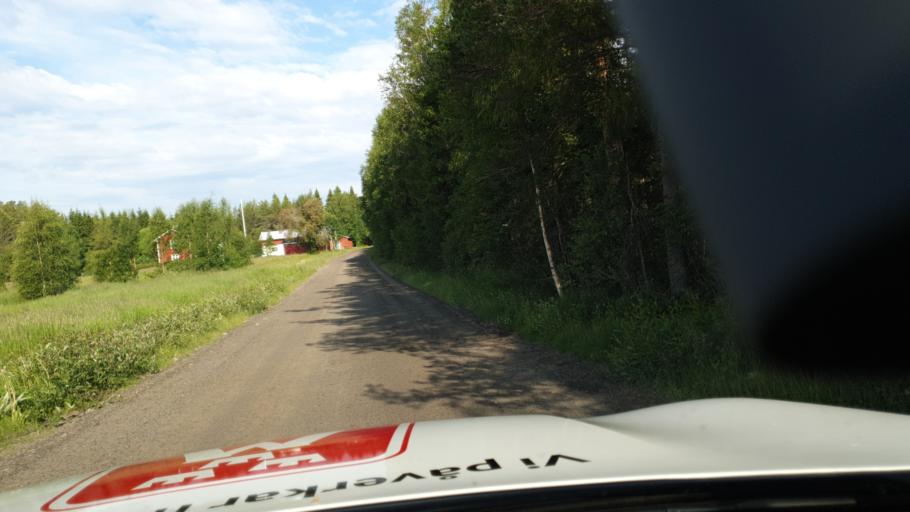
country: SE
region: Vaesterbotten
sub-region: Robertsfors Kommun
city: Robertsfors
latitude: 64.2273
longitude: 21.0582
